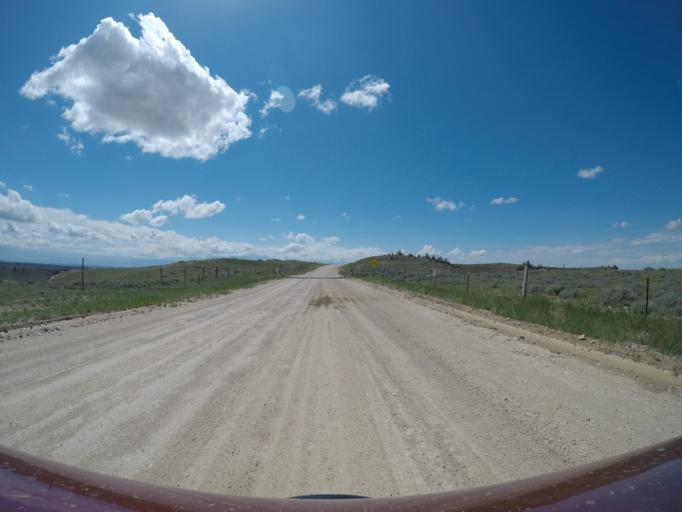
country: US
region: Wyoming
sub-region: Park County
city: Powell
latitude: 45.2065
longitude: -108.7699
